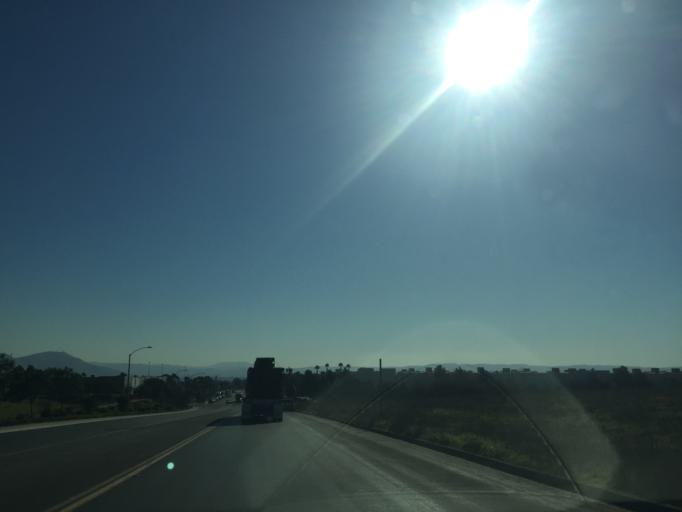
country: MX
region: Baja California
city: Tijuana
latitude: 32.5622
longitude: -116.9280
